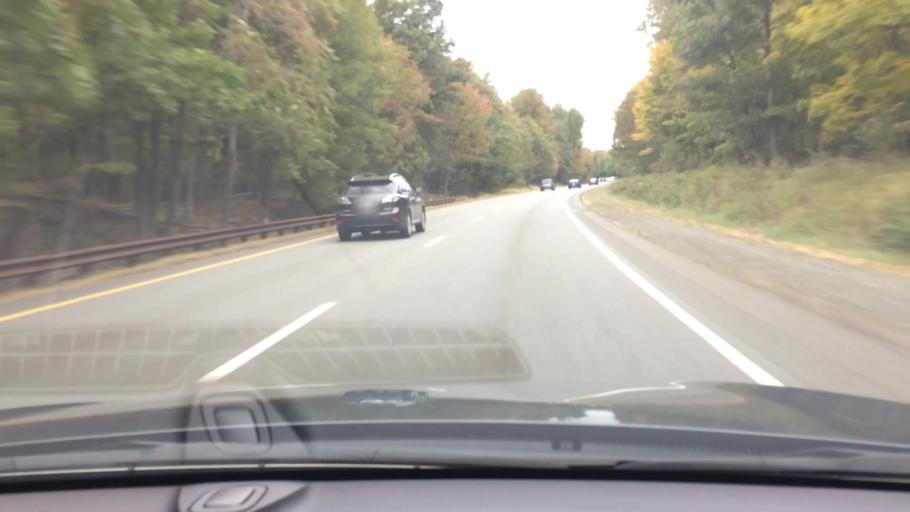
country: US
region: New Jersey
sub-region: Bergen County
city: Alpine
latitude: 40.9643
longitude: -73.9170
